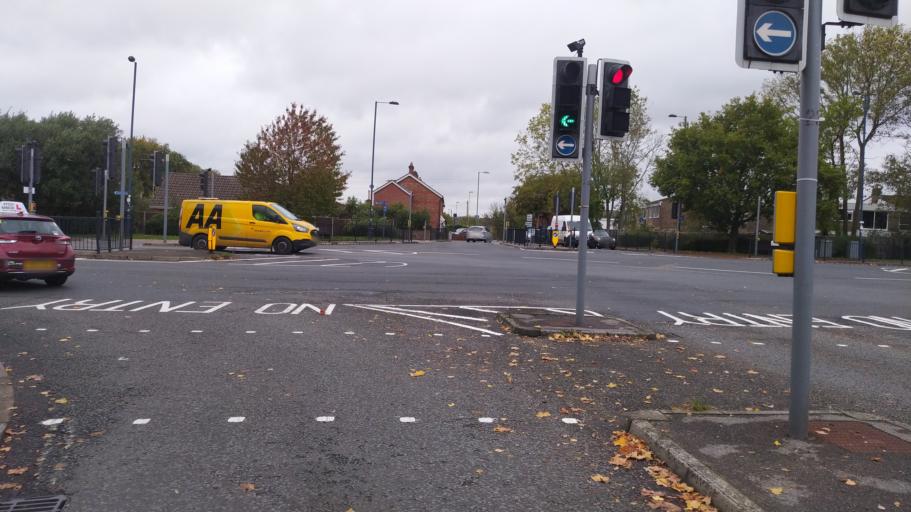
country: GB
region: England
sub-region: Hampshire
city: Cowplain
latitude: 50.9081
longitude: -1.0080
